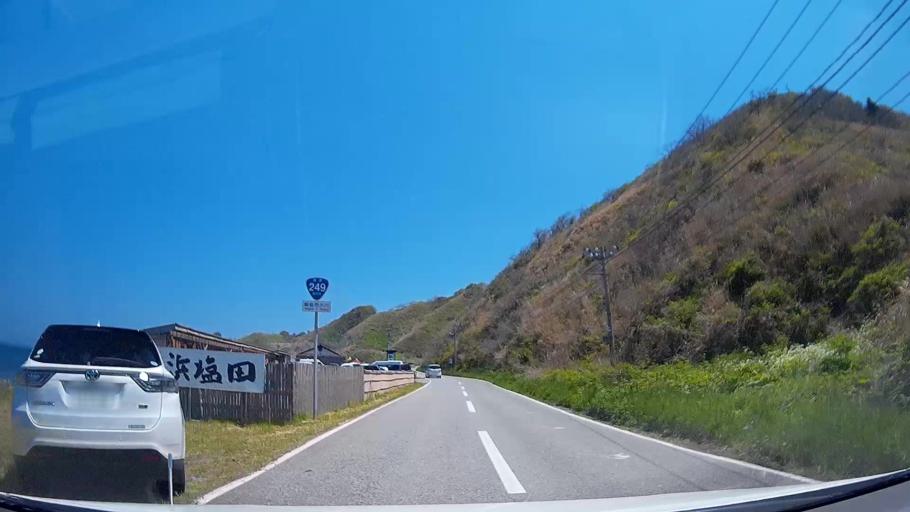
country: JP
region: Ishikawa
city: Nanao
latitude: 37.4419
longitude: 137.0429
